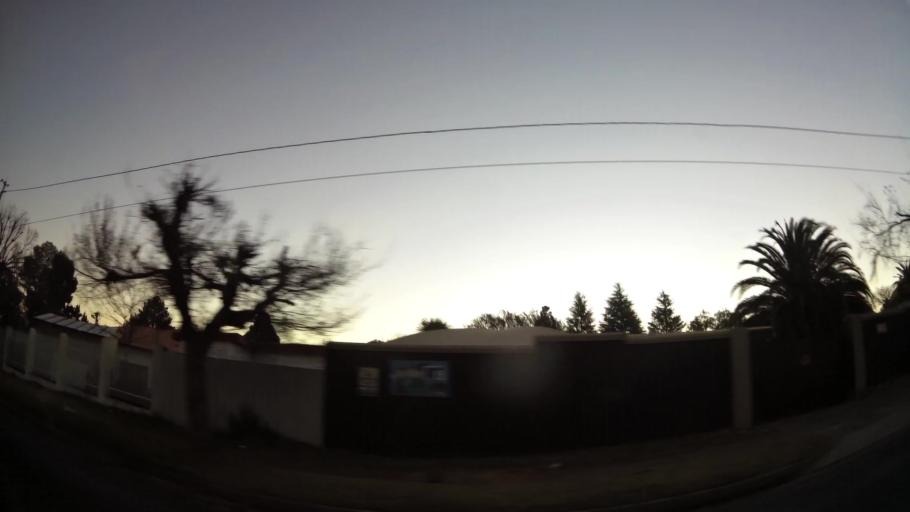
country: ZA
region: Gauteng
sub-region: City of Johannesburg Metropolitan Municipality
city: Roodepoort
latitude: -26.1741
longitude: 27.9234
